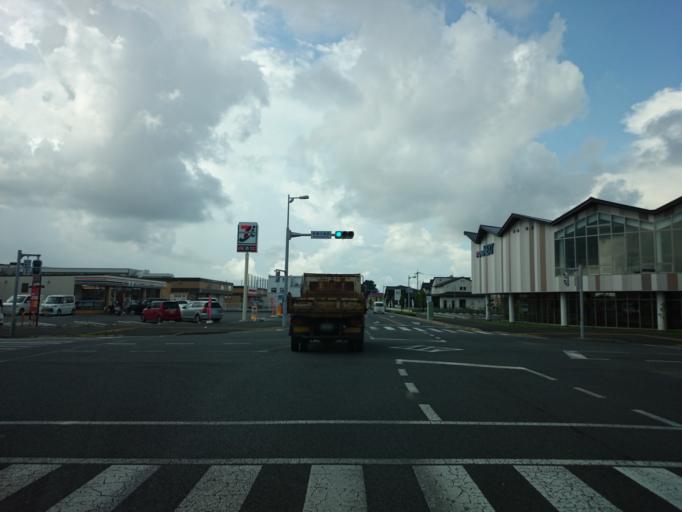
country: JP
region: Ibaraki
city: Naka
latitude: 36.0986
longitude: 140.0760
